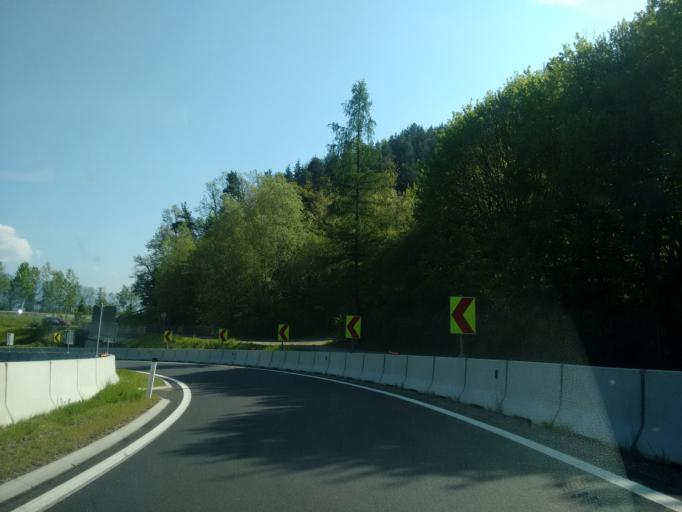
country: AT
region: Styria
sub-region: Politischer Bezirk Bruck-Muerzzuschlag
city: Frauenberg
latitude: 47.4472
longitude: 15.3266
